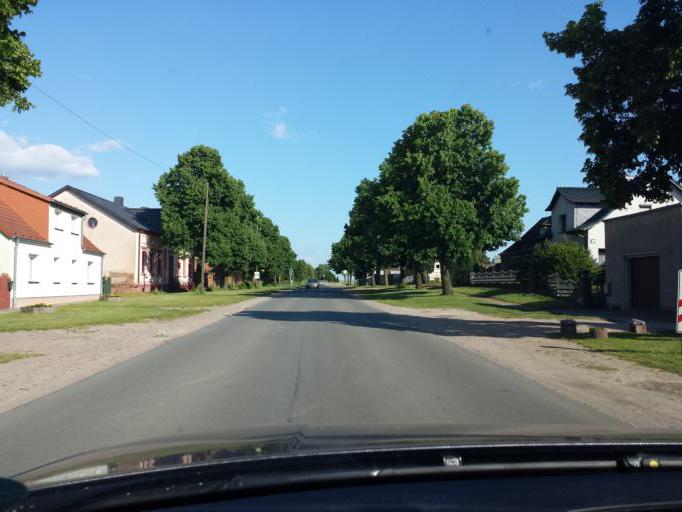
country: DE
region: Brandenburg
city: Neuruppin
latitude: 52.9070
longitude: 12.8420
